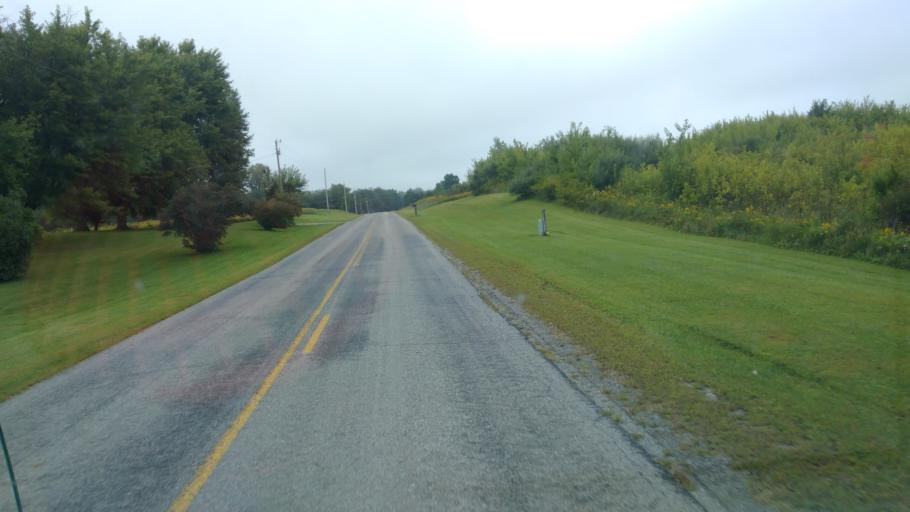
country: US
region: Ohio
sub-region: Hardin County
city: Kenton
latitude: 40.5712
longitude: -83.6340
